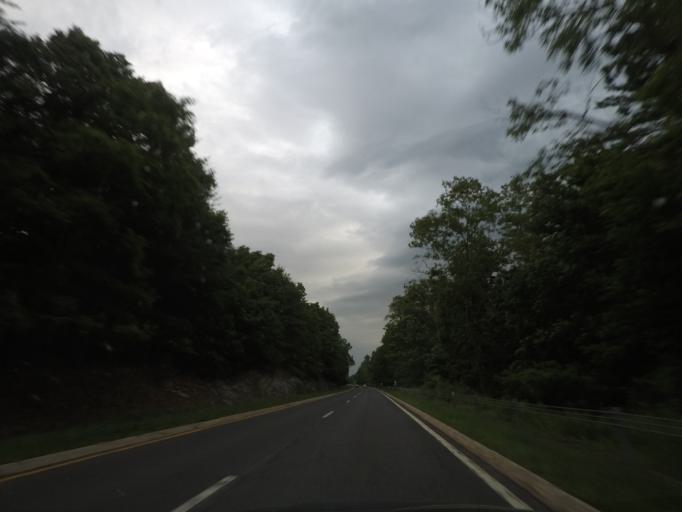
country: US
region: New York
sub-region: Columbia County
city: Philmont
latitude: 42.2370
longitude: -73.6234
